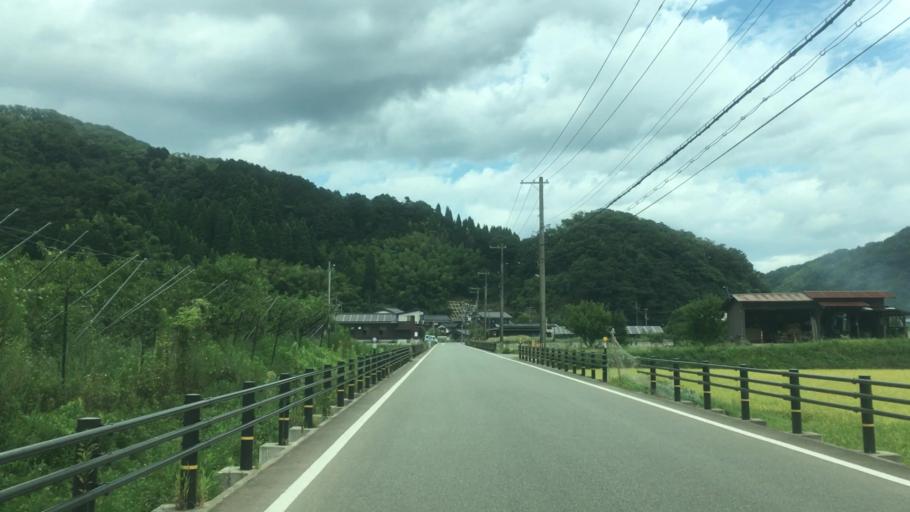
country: JP
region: Hyogo
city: Toyooka
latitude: 35.5913
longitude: 134.7983
